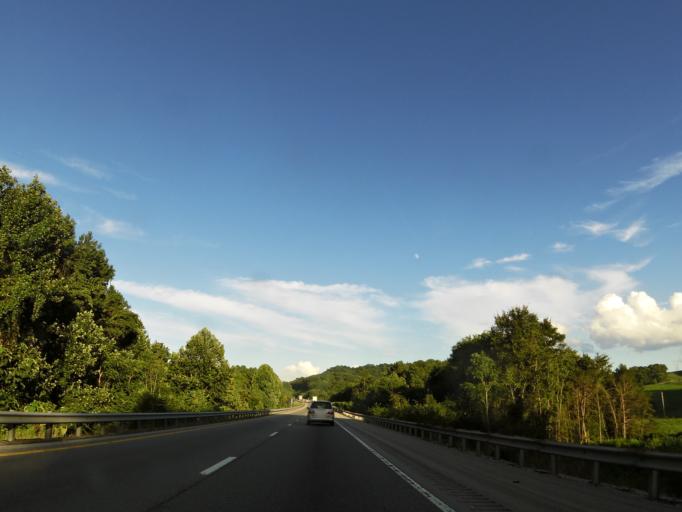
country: US
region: Tennessee
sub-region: Smith County
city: Gordonsville
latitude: 36.1438
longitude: -85.8474
